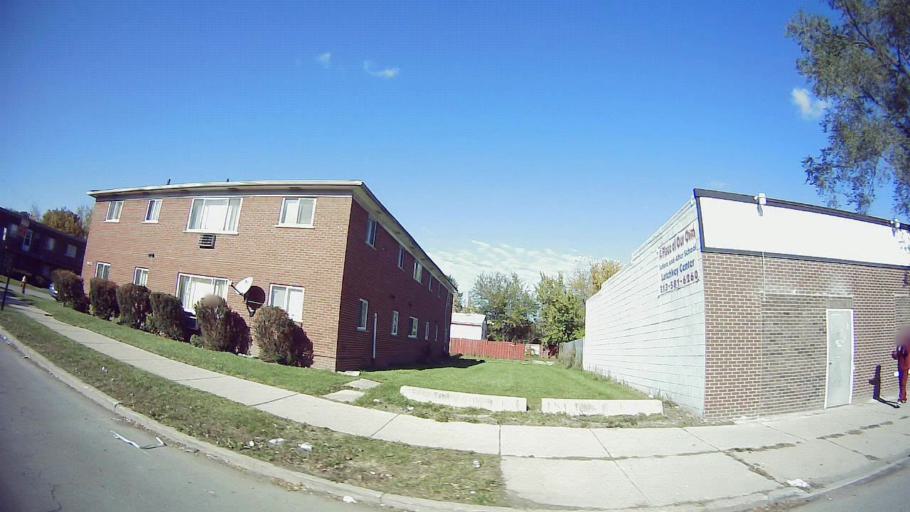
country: US
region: Michigan
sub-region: Wayne County
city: Dearborn
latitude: 42.3509
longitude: -83.1936
